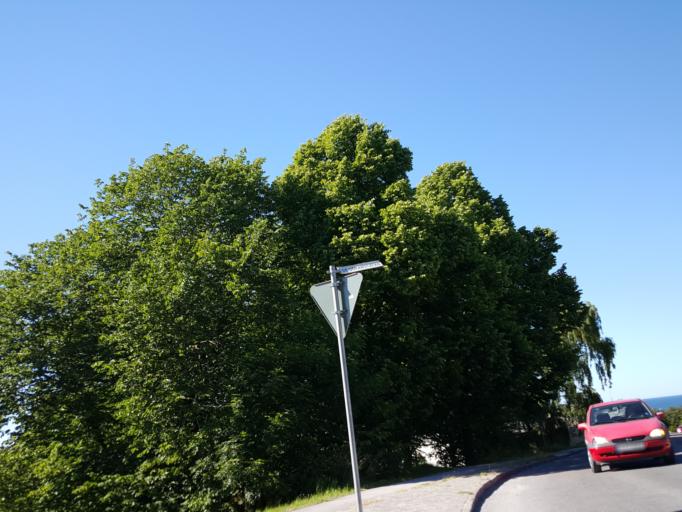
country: SE
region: Gotland
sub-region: Gotland
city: Visby
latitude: 57.6450
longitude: 18.3017
